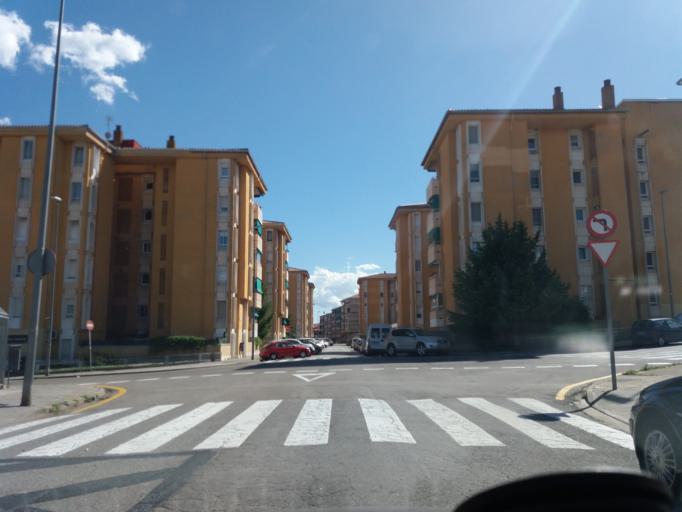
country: ES
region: Catalonia
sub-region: Provincia de Barcelona
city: Manresa
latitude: 41.7414
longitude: 1.8353
